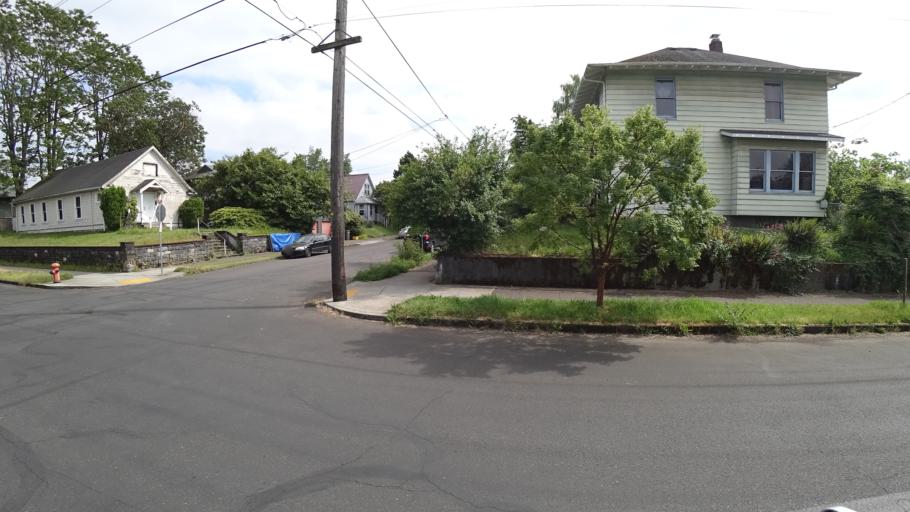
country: US
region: Oregon
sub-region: Multnomah County
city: Portland
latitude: 45.5564
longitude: -122.6450
